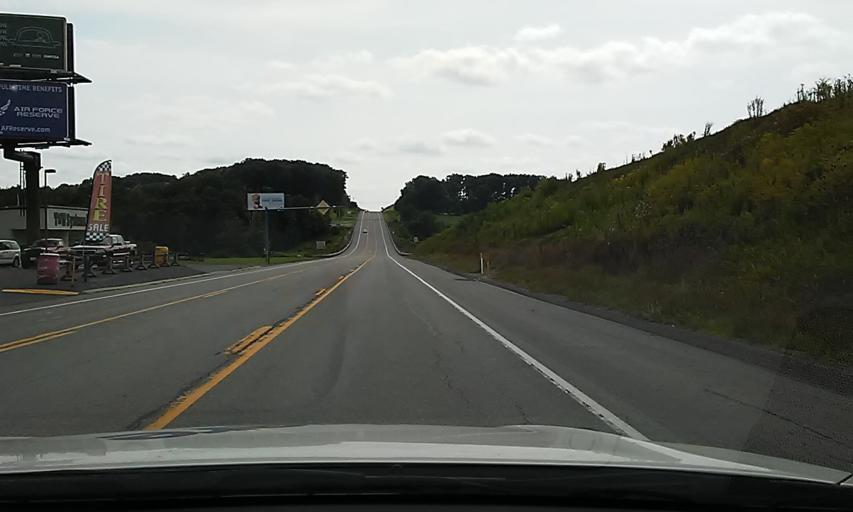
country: US
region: Pennsylvania
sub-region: Jefferson County
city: Punxsutawney
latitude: 40.9257
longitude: -78.9845
